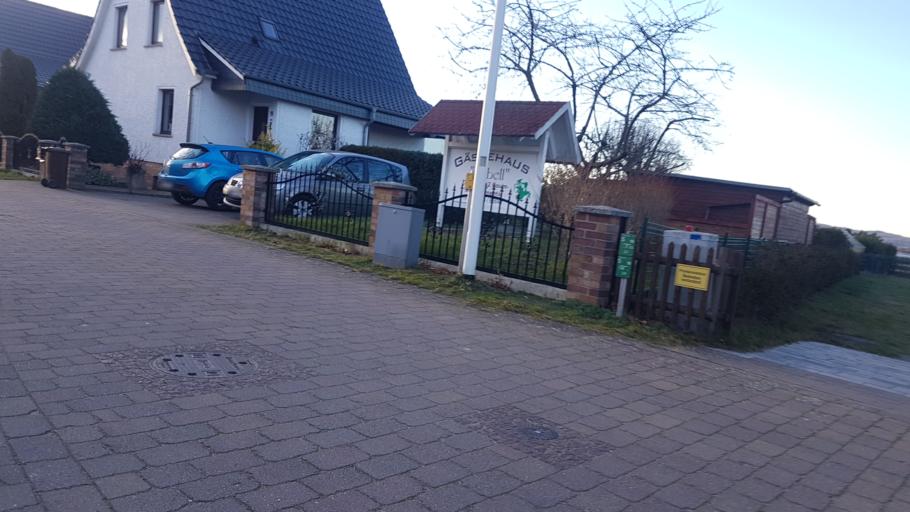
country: DE
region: Mecklenburg-Vorpommern
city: Ostseebad Sellin
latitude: 54.3600
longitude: 13.7019
